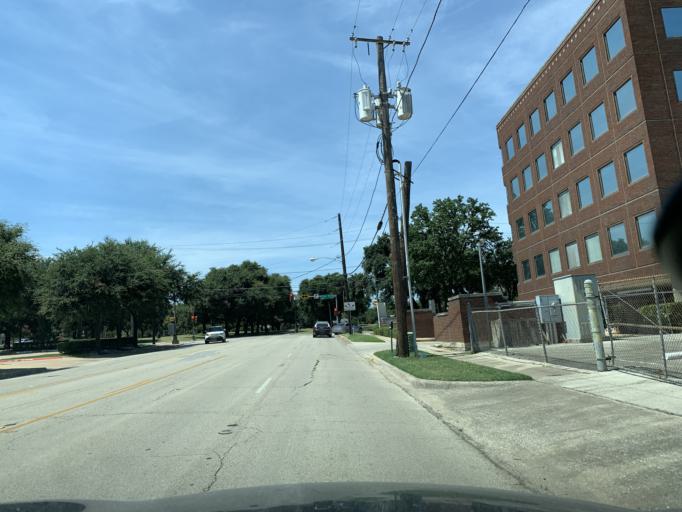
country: US
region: Texas
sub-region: Dallas County
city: Dallas
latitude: 32.7917
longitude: -96.7845
